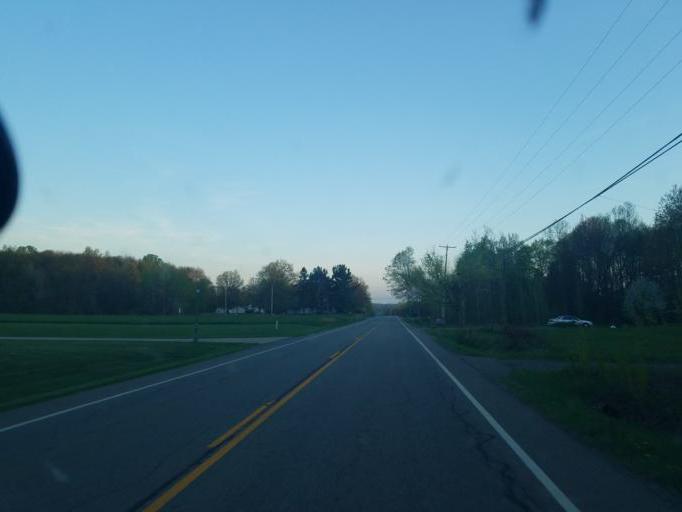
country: US
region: Ohio
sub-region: Trumbull County
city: Brookfield Center
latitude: 41.2888
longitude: -80.5685
